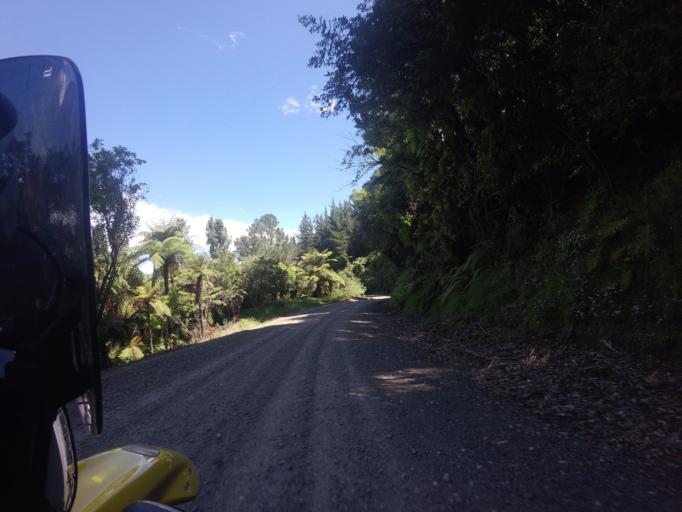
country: NZ
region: Hawke's Bay
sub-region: Wairoa District
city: Wairoa
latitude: -38.9803
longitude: 177.7036
